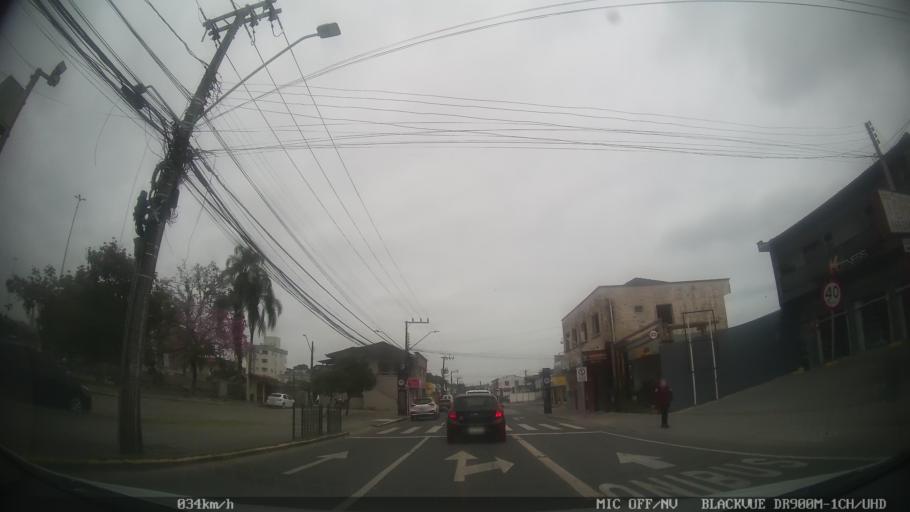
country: BR
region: Santa Catarina
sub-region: Joinville
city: Joinville
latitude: -26.3358
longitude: -48.8475
